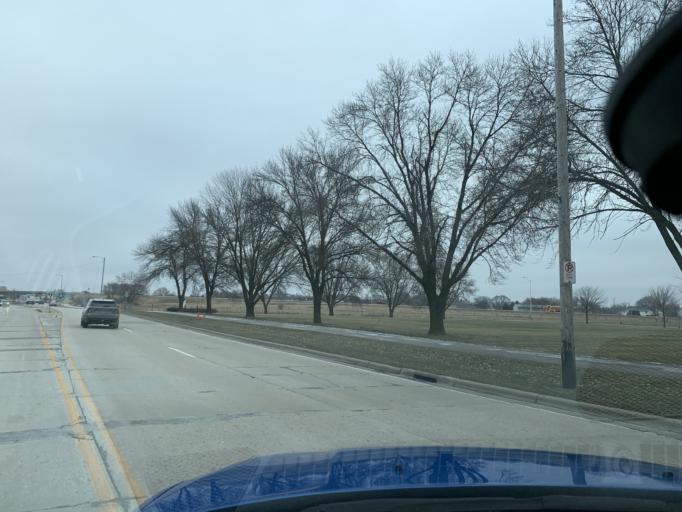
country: US
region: Wisconsin
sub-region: Dane County
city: Sun Prairie
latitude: 43.1875
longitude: -89.2383
